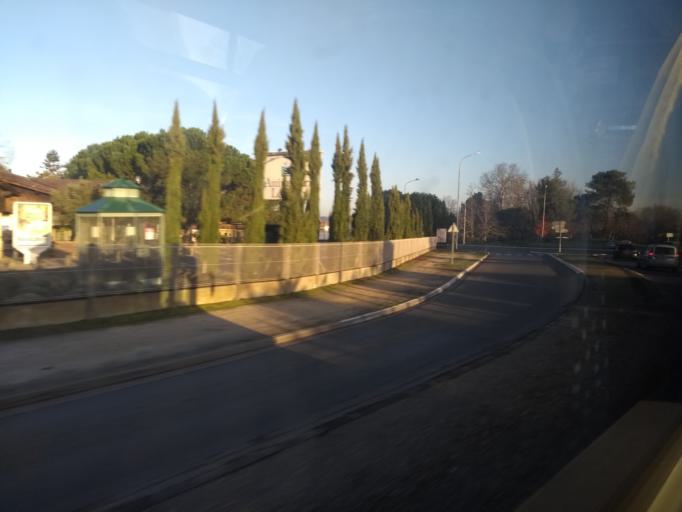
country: FR
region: Aquitaine
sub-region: Departement de la Gironde
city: Canejan
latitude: 44.7597
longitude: -0.6235
